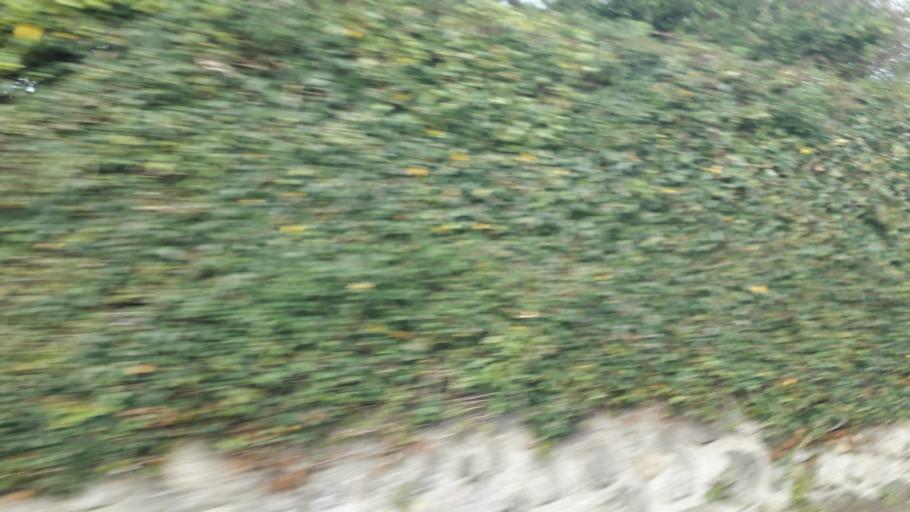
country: IE
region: Leinster
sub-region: Lu
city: Blackrock
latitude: 54.0161
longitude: -6.3108
